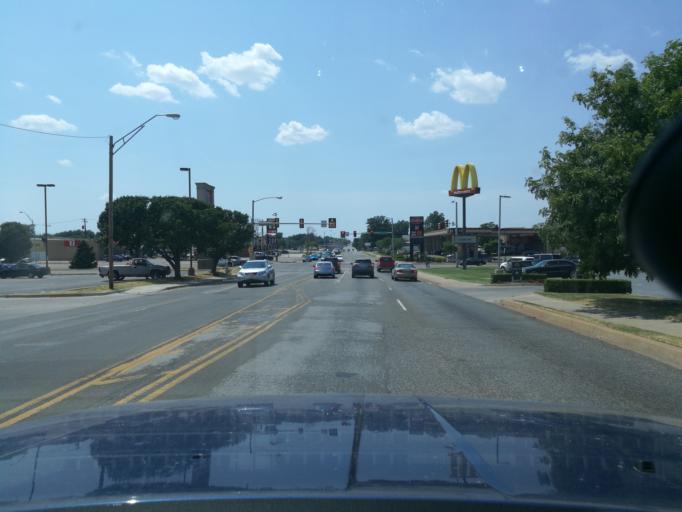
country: US
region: Oklahoma
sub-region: Oklahoma County
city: Oklahoma City
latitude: 35.4208
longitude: -97.5070
